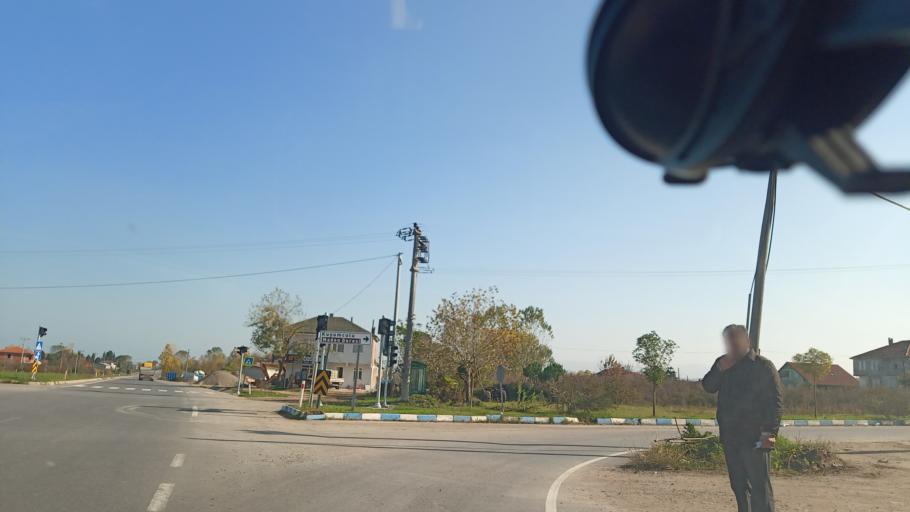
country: TR
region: Sakarya
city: Karasu
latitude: 41.0696
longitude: 30.8028
